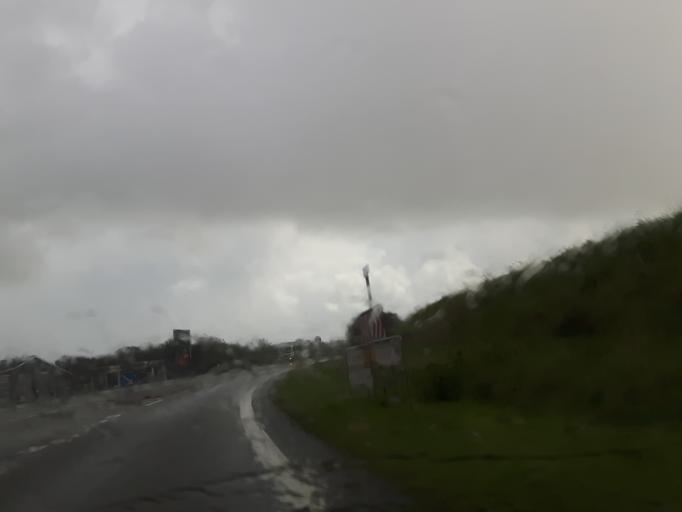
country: DK
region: North Denmark
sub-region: Thisted Kommune
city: Hurup
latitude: 56.6370
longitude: 8.5109
